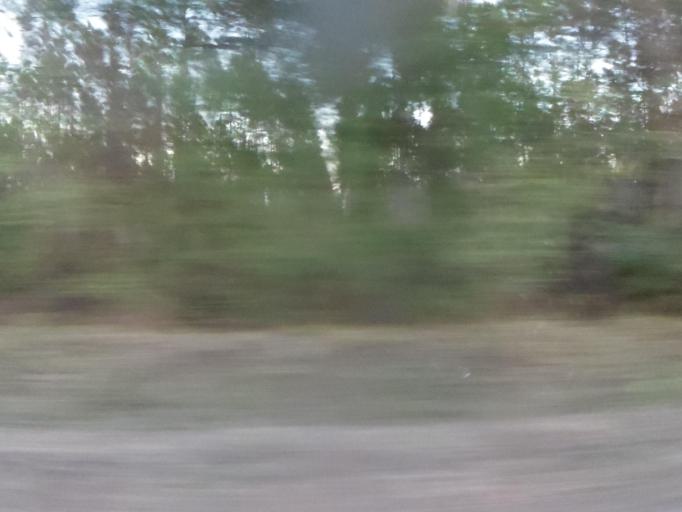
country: US
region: Florida
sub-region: Clay County
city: Asbury Lake
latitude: 29.9690
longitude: -81.7939
